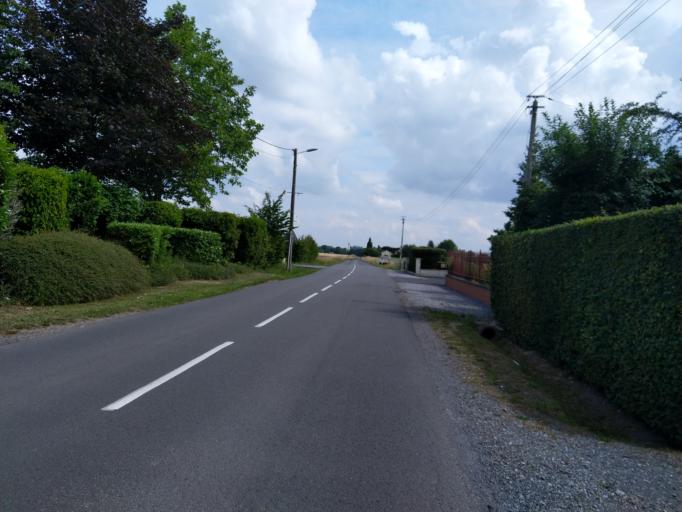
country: FR
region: Nord-Pas-de-Calais
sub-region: Departement du Nord
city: Rousies
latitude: 50.3078
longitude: 3.9975
